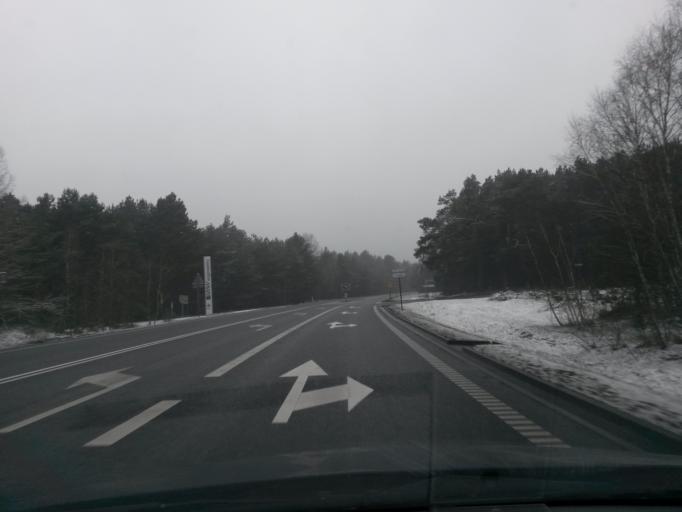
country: PL
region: Kujawsko-Pomorskie
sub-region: Powiat bydgoski
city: Solec Kujawski
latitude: 53.0592
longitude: 18.2296
